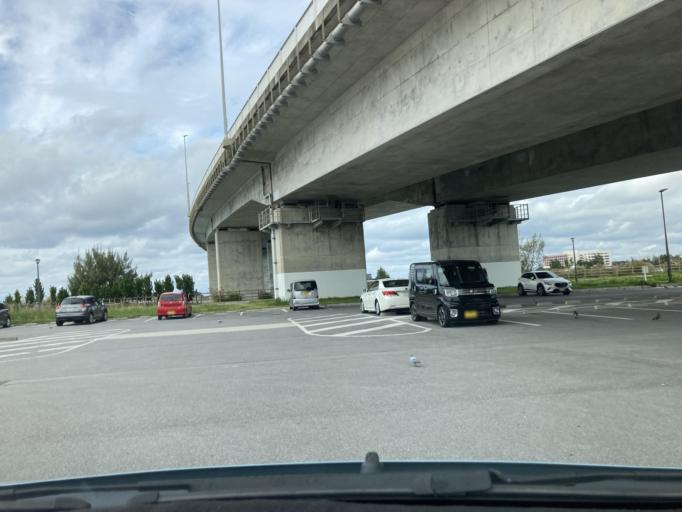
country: JP
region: Okinawa
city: Tomigusuku
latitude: 26.1619
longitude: 127.6529
